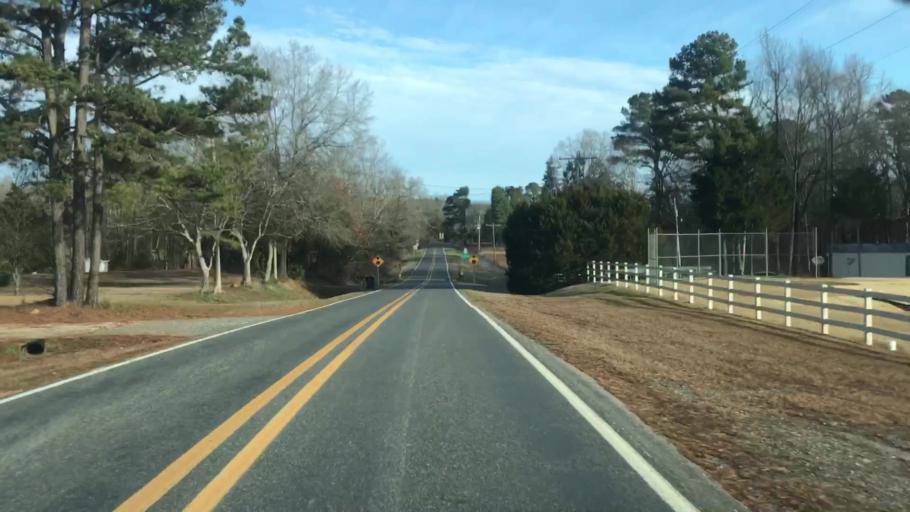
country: US
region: Arkansas
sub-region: Garland County
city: Rockwell
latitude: 34.5077
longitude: -93.2761
